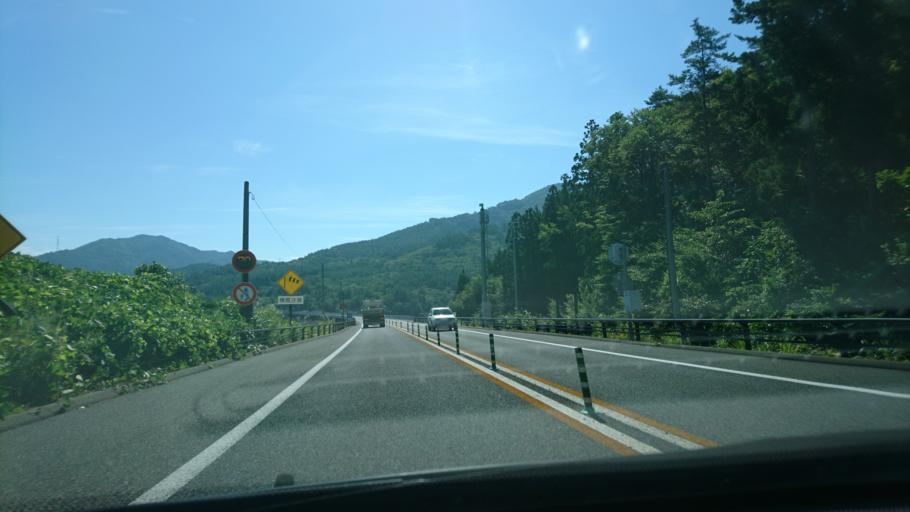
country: JP
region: Iwate
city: Kitakami
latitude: 39.2906
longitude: 141.3211
